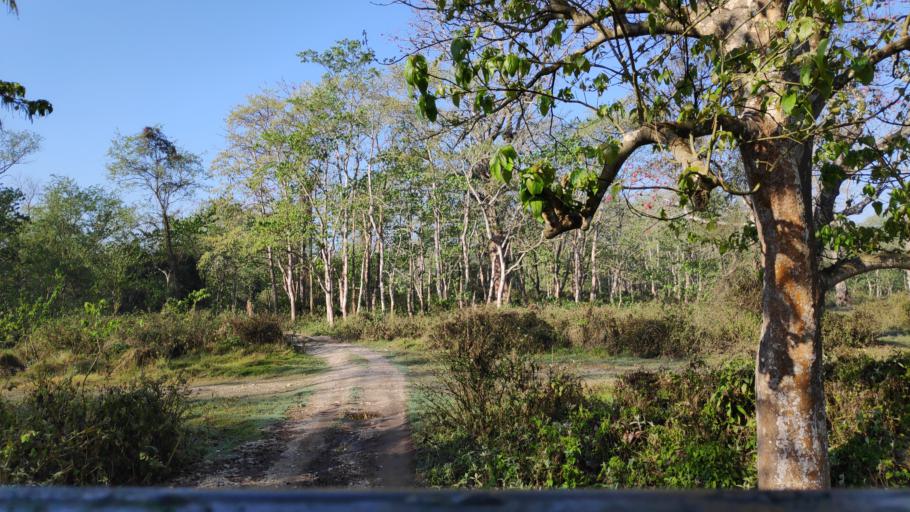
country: NP
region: Central Region
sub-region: Narayani Zone
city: Bharatpur
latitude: 27.5579
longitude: 84.5573
